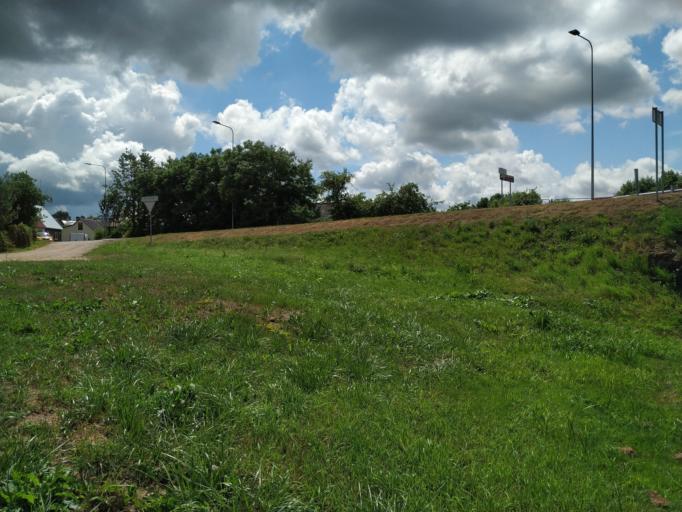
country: LT
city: Kupiskis
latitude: 55.8437
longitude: 24.9679
